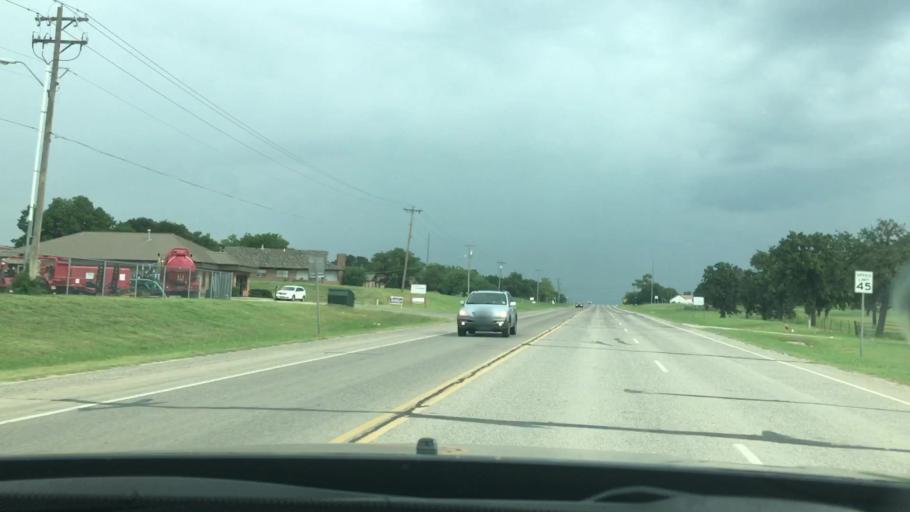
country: US
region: Oklahoma
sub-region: Carter County
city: Healdton
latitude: 34.2129
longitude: -97.4748
